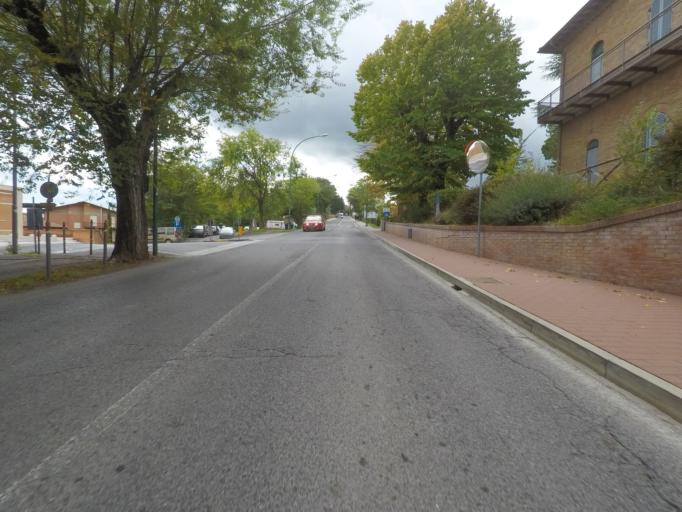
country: IT
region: Tuscany
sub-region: Provincia di Siena
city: Montepulciano
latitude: 43.1013
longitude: 11.7856
